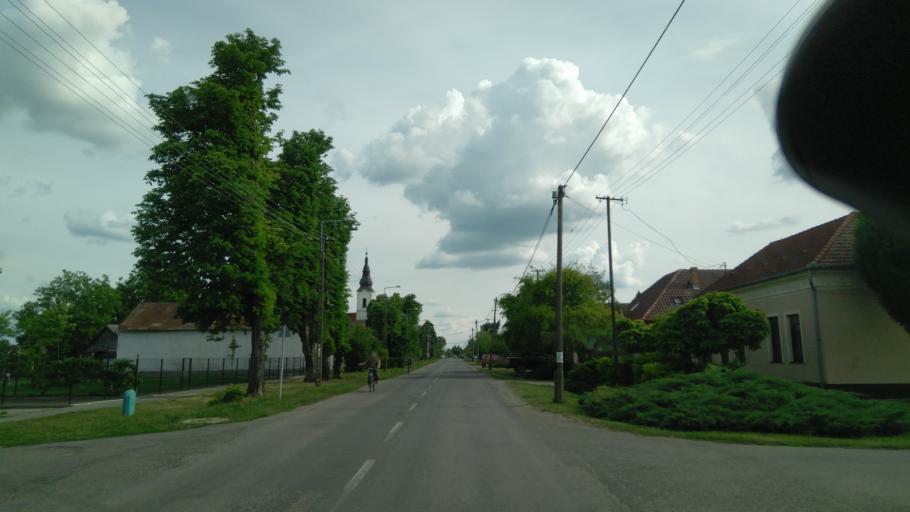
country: HU
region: Bekes
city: Battonya
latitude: 46.2907
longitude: 21.0171
